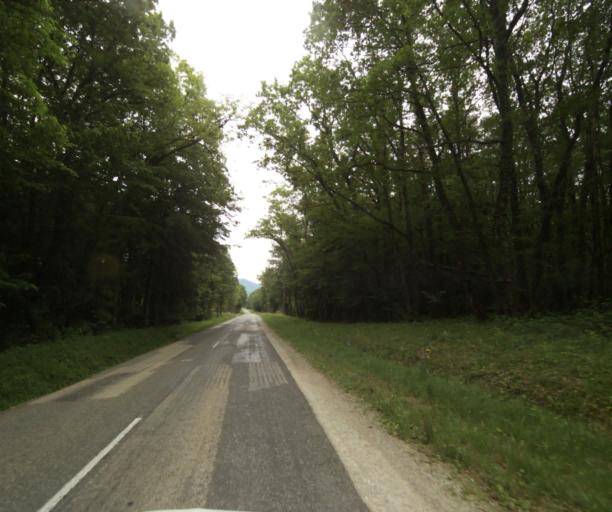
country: FR
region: Rhone-Alpes
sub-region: Departement de la Haute-Savoie
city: Sciez
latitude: 46.3166
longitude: 6.3987
